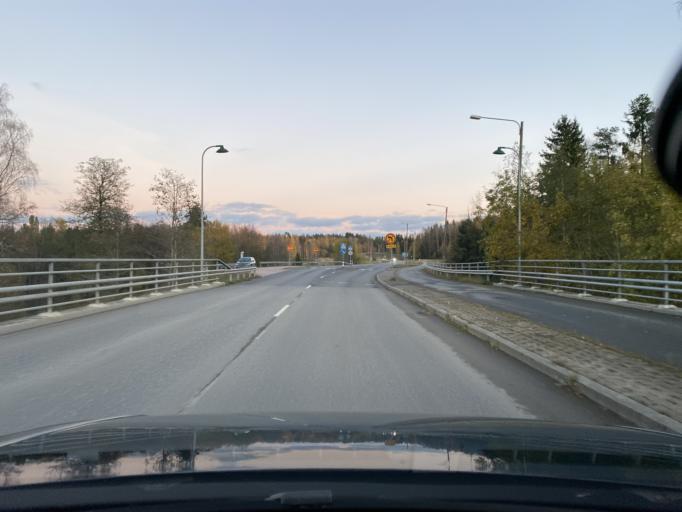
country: FI
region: Pirkanmaa
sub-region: Tampere
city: Lempaeaelae
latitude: 61.3282
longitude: 23.7657
